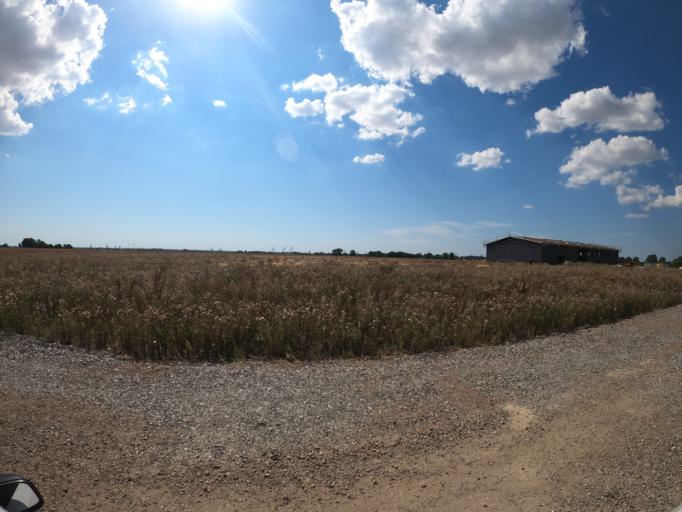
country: SE
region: Skane
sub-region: Lunds Kommun
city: Lund
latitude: 55.6827
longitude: 13.2117
